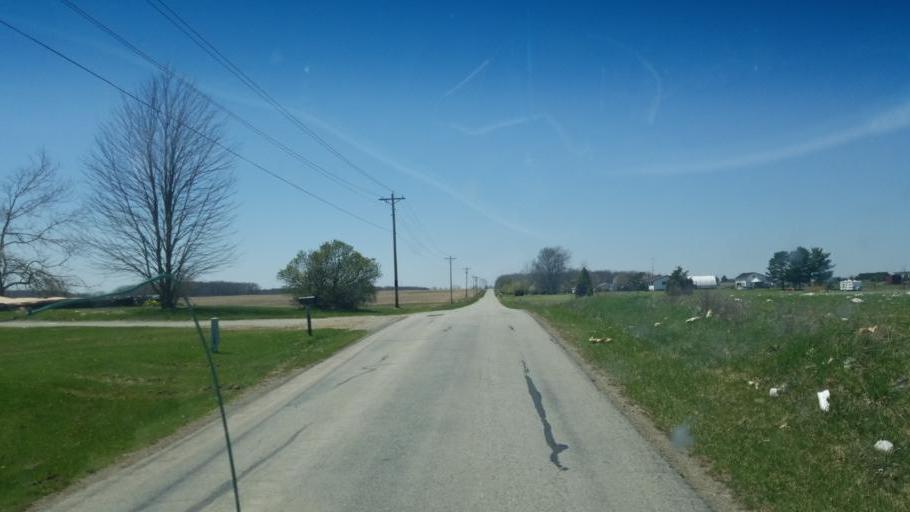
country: US
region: Ohio
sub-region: Huron County
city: Greenwich
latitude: 41.0935
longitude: -82.5050
